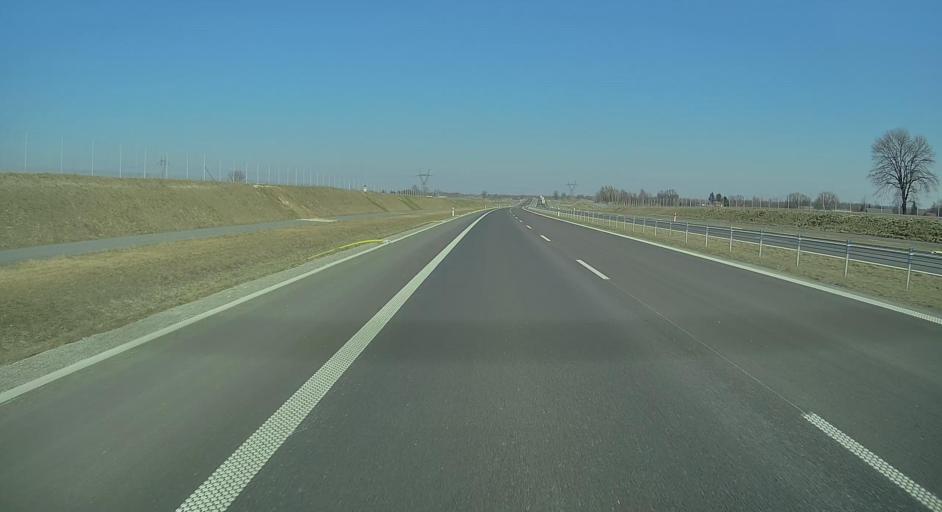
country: PL
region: Lublin Voivodeship
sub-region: Powiat janowski
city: Modliborzyce
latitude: 50.7946
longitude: 22.2934
